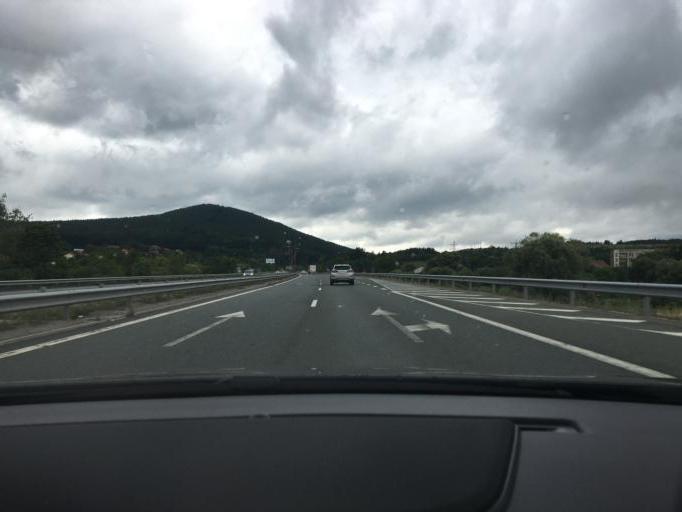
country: BG
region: Pernik
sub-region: Obshtina Pernik
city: Pernik
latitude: 42.5368
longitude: 23.1310
